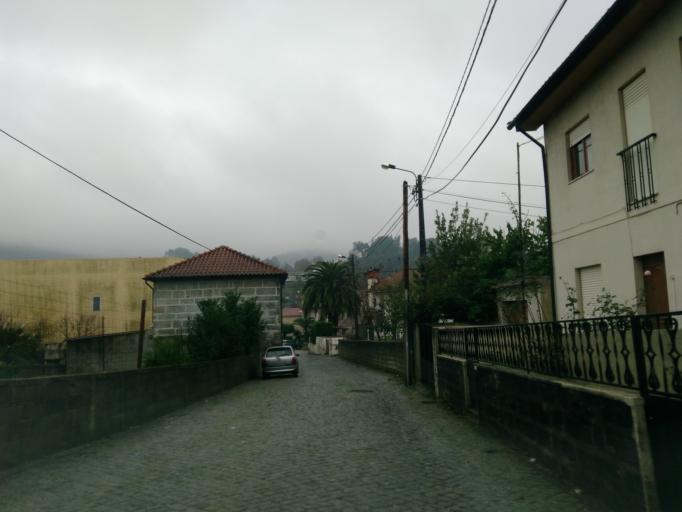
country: PT
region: Braga
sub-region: Braga
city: Adaufe
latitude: 41.5610
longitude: -8.3915
